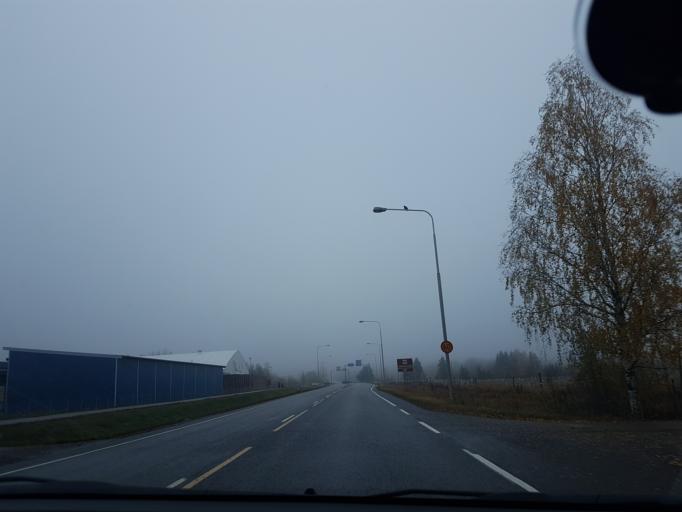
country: FI
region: Uusimaa
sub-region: Helsinki
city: Jaervenpaeae
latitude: 60.4676
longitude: 25.1408
